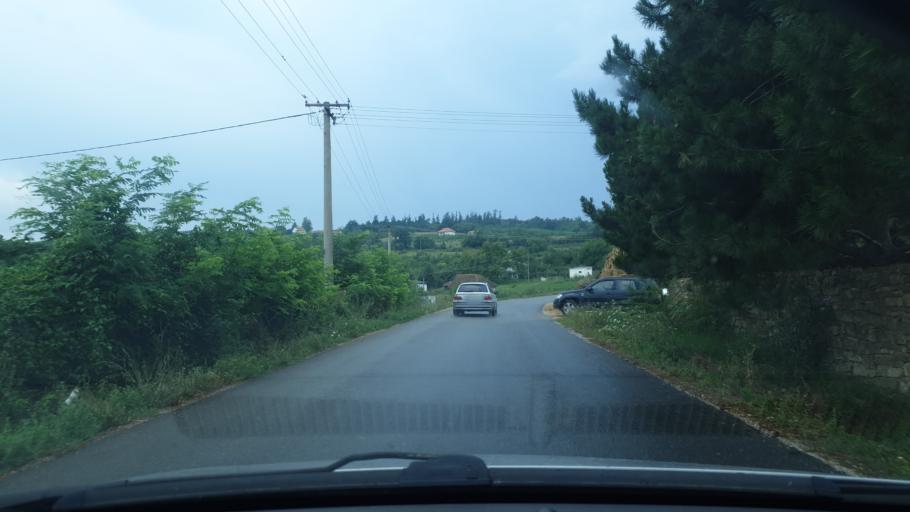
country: RS
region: Central Serbia
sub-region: Sumadijski Okrug
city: Kragujevac
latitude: 44.0632
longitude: 20.7898
